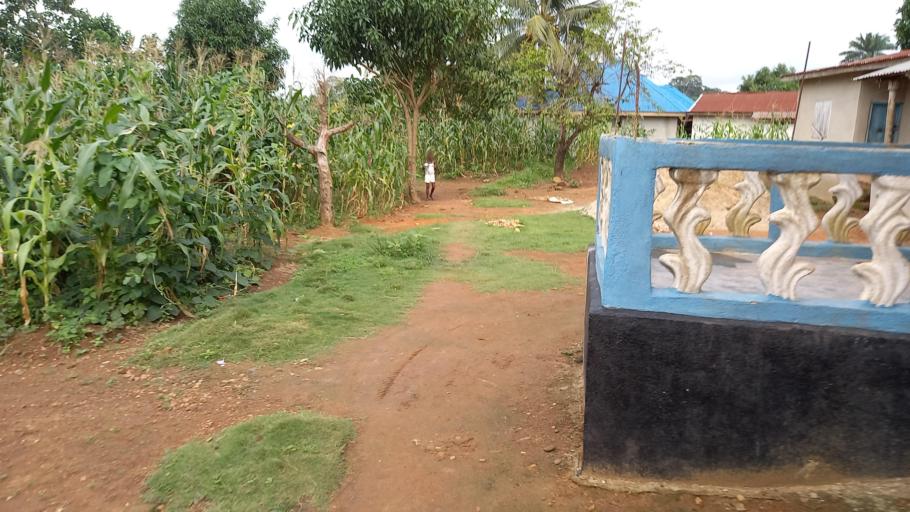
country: SL
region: Eastern Province
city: Kailahun
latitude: 8.2816
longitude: -10.5758
